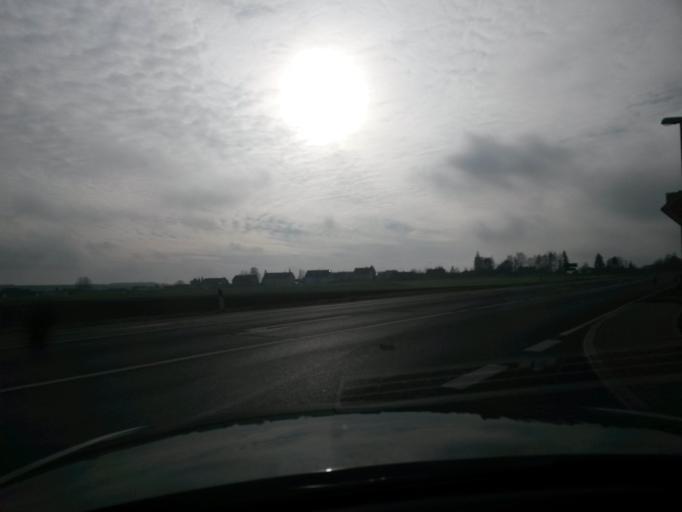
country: DE
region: Bavaria
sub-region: Regierungsbezirk Unterfranken
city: Kurnach
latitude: 49.8497
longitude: 10.0290
